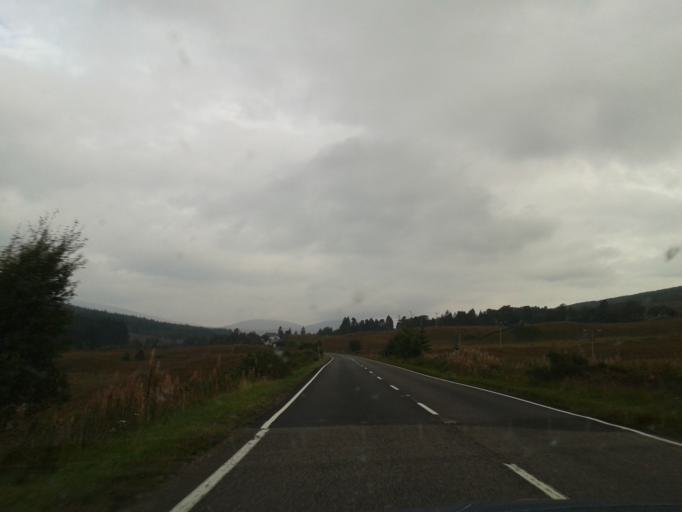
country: GB
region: Scotland
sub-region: Highland
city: Spean Bridge
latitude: 56.5111
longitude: -4.7682
